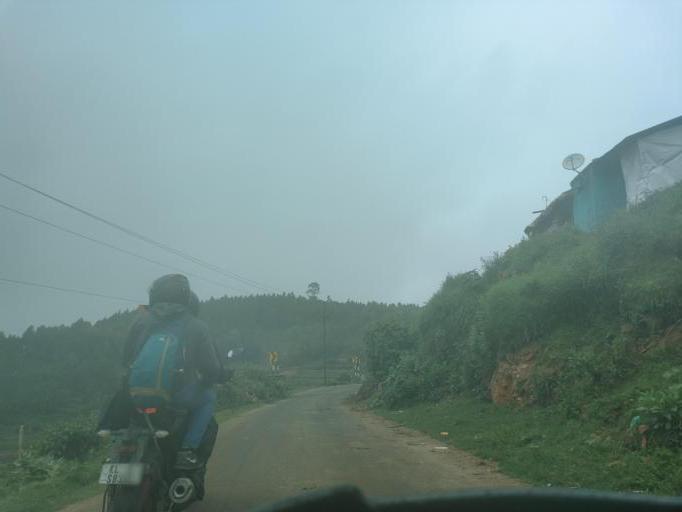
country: IN
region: Tamil Nadu
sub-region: Dindigul
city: Kodaikanal
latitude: 10.2233
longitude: 77.3480
